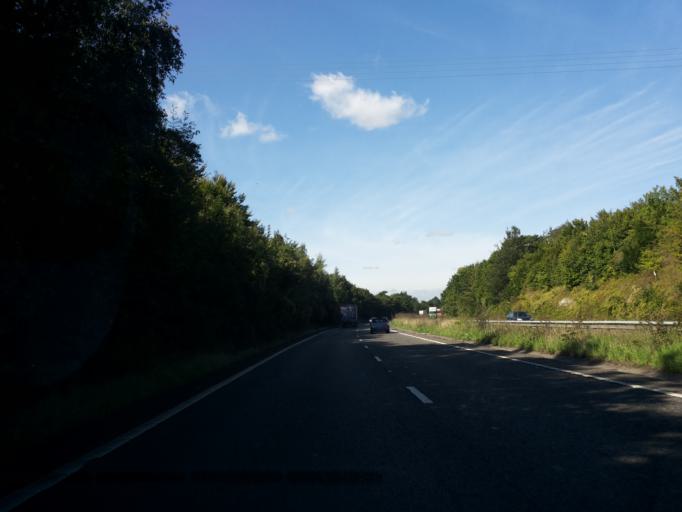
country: GB
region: England
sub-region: Kent
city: Canterbury
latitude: 51.2554
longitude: 1.0825
